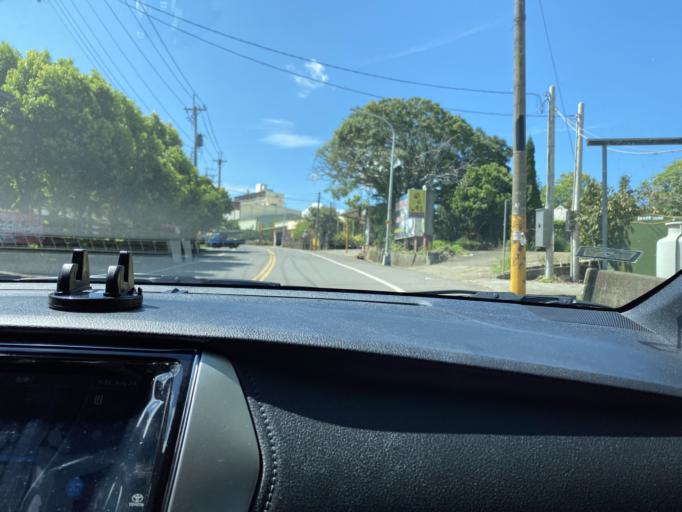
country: TW
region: Taiwan
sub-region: Nantou
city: Nantou
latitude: 23.8490
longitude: 120.6288
